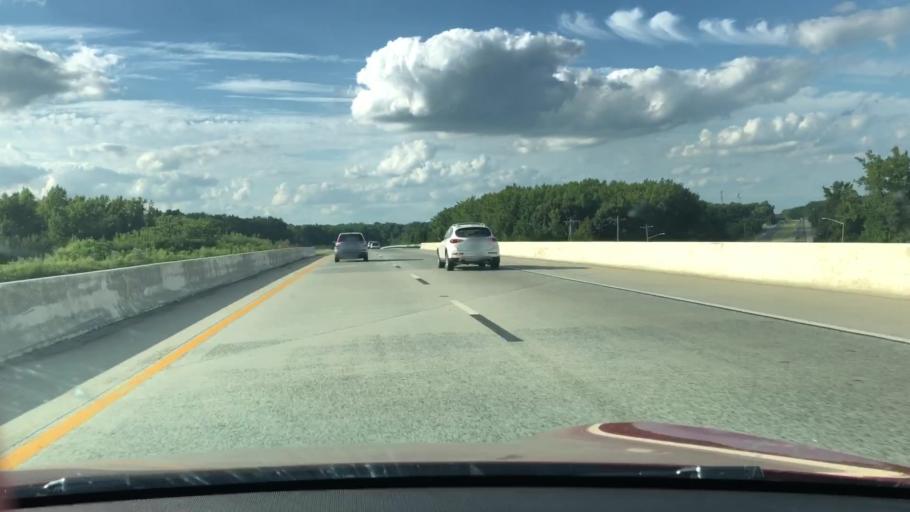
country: US
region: Delaware
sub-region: New Castle County
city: Townsend
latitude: 39.3860
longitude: -75.6641
